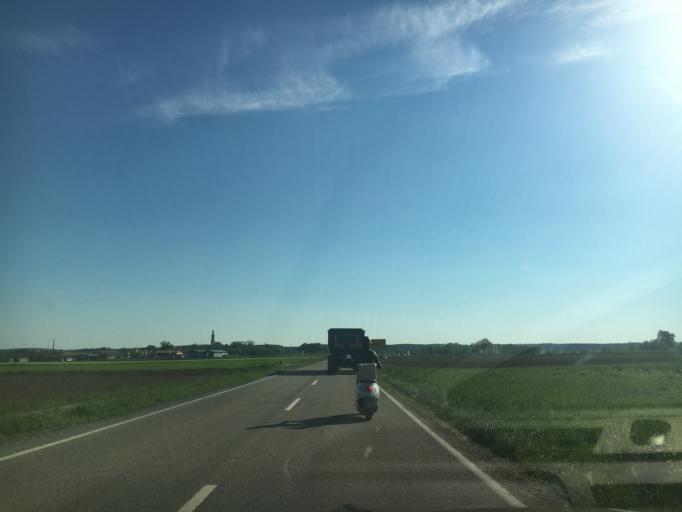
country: DE
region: Bavaria
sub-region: Upper Bavaria
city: Nussdorf
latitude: 47.9295
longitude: 12.5920
